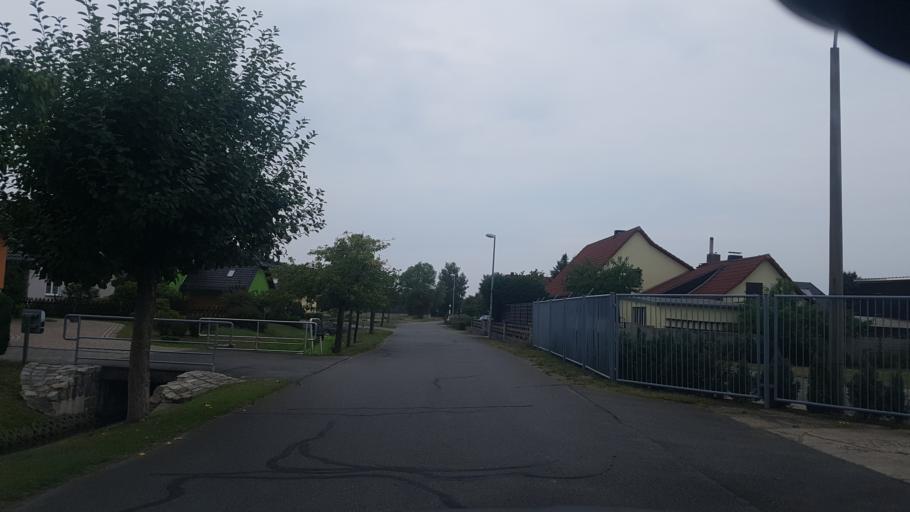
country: DE
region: Brandenburg
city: Guteborn
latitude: 51.4269
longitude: 13.9144
